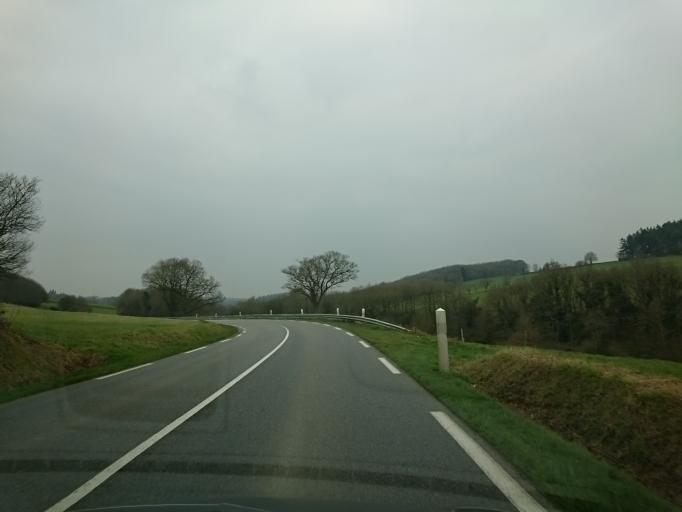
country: FR
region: Brittany
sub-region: Departement d'Ille-et-Vilaine
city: Pance
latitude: 47.8850
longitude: -1.6224
